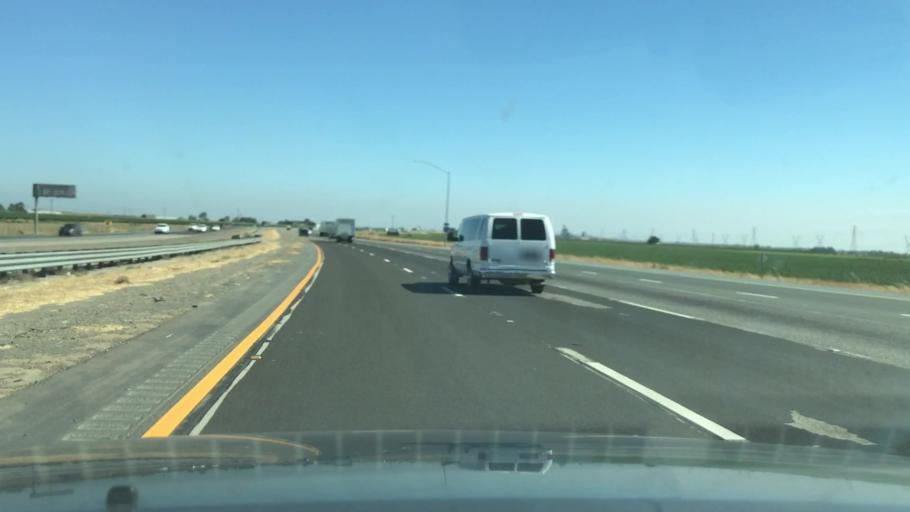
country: US
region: California
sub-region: San Joaquin County
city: Woodbridge
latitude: 38.1123
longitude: -121.3961
